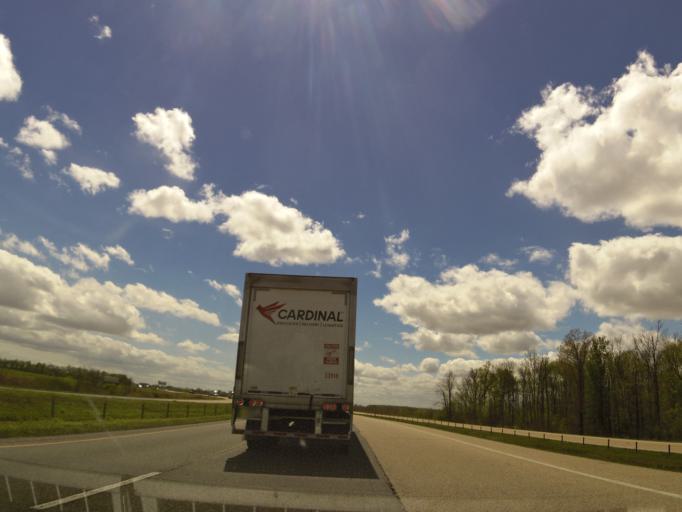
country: US
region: Arkansas
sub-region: Crittenden County
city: Marion
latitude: 35.3886
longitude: -90.2781
